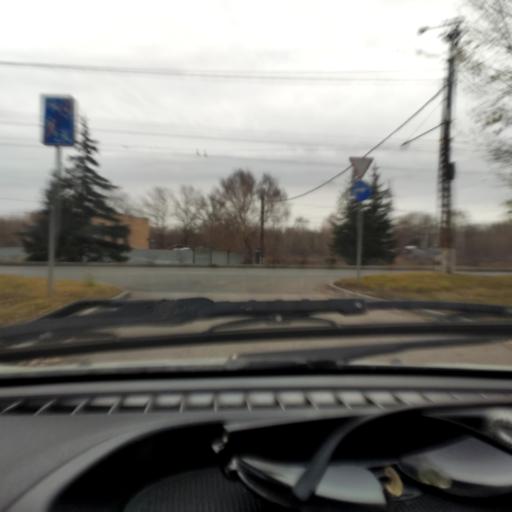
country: RU
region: Samara
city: Tol'yatti
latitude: 53.5092
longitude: 49.4543
